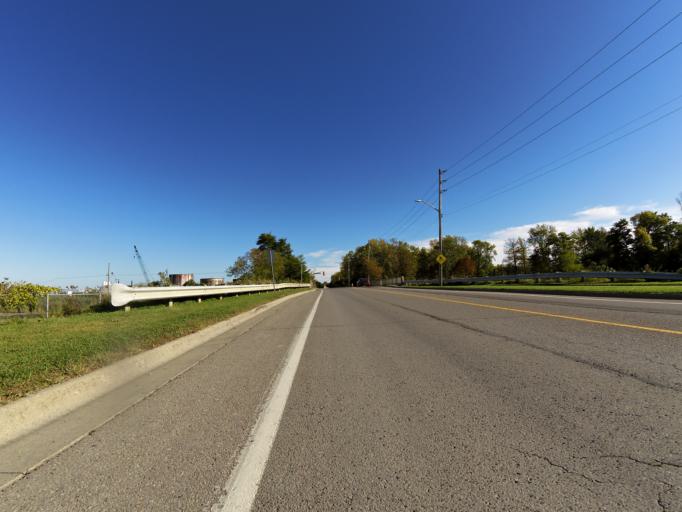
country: CA
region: Ontario
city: Oshawa
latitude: 43.8669
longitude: -78.8314
